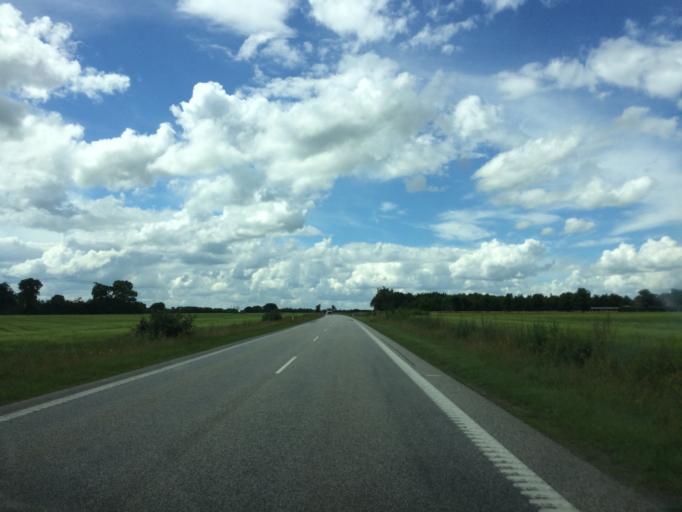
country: DK
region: North Denmark
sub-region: Vesthimmerland Kommune
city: Alestrup
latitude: 56.6210
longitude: 9.5808
